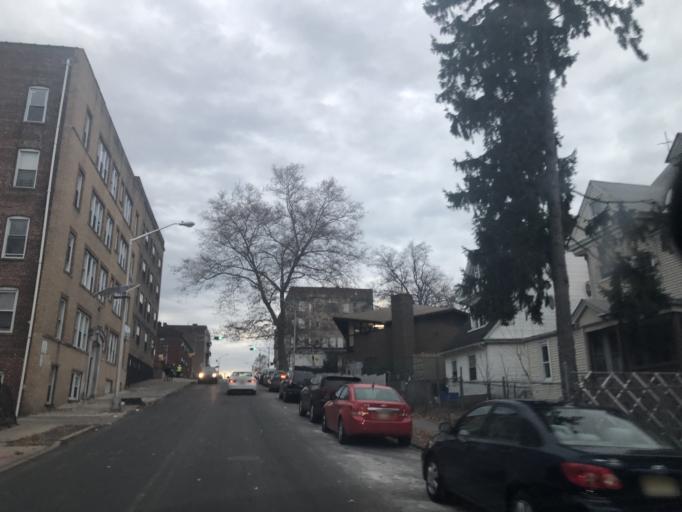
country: US
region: New Jersey
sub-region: Essex County
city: East Orange
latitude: 40.7636
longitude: -74.2079
